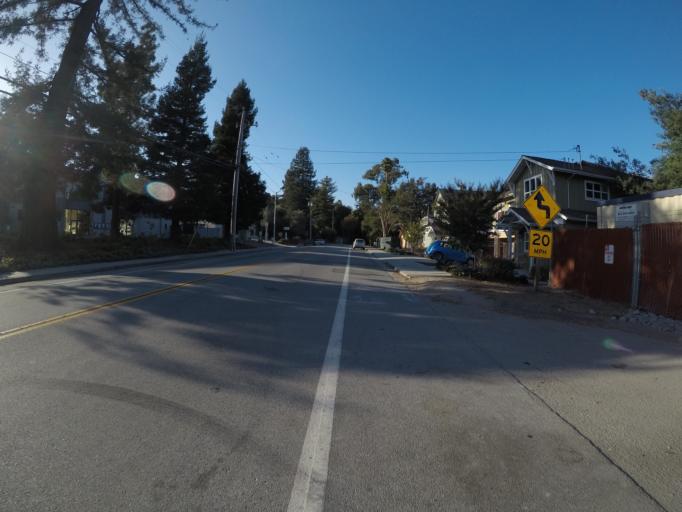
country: US
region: California
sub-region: Santa Cruz County
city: Pasatiempo
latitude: 36.9908
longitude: -122.0321
